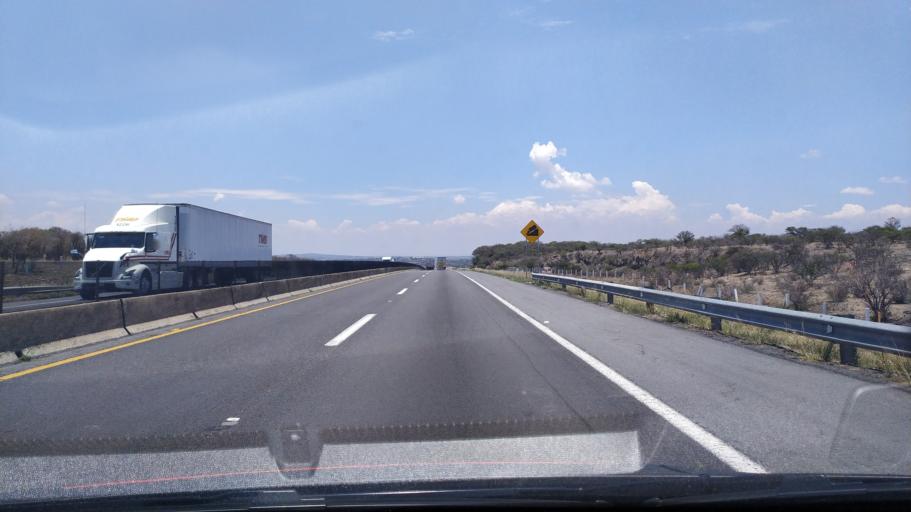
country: MX
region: Jalisco
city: Jalostotitlan
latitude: 21.0852
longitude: -102.4910
